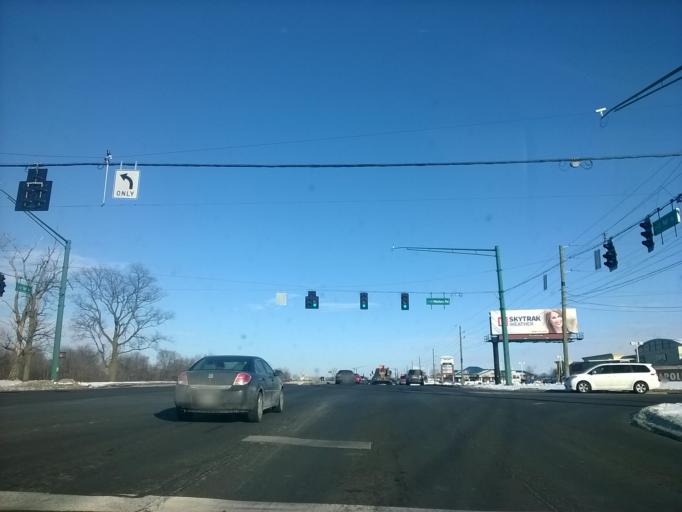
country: US
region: Indiana
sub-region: Hamilton County
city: Fishers
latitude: 39.9270
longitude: -86.0467
